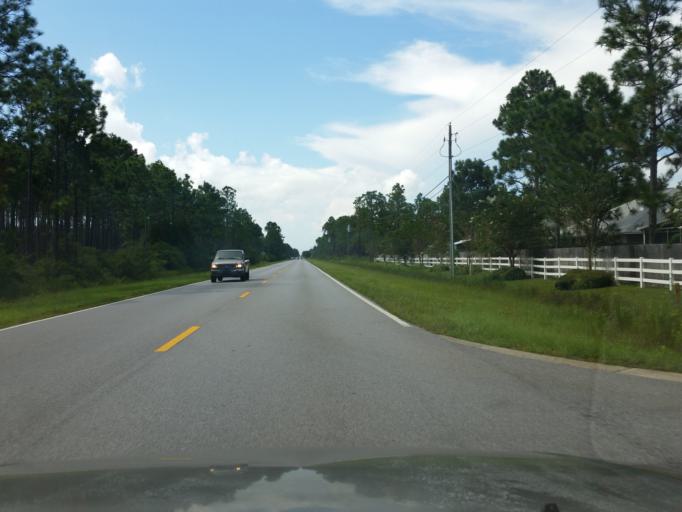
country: US
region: Florida
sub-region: Escambia County
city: Myrtle Grove
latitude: 30.3654
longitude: -87.4026
